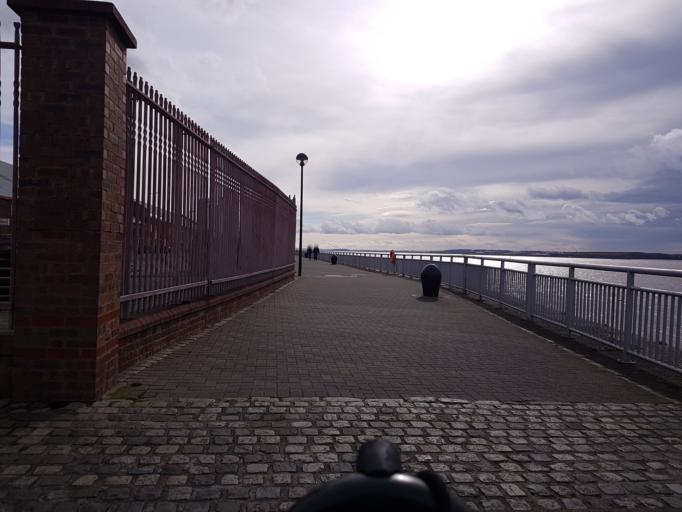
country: GB
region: England
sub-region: Liverpool
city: Liverpool
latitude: 53.3850
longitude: -2.9830
